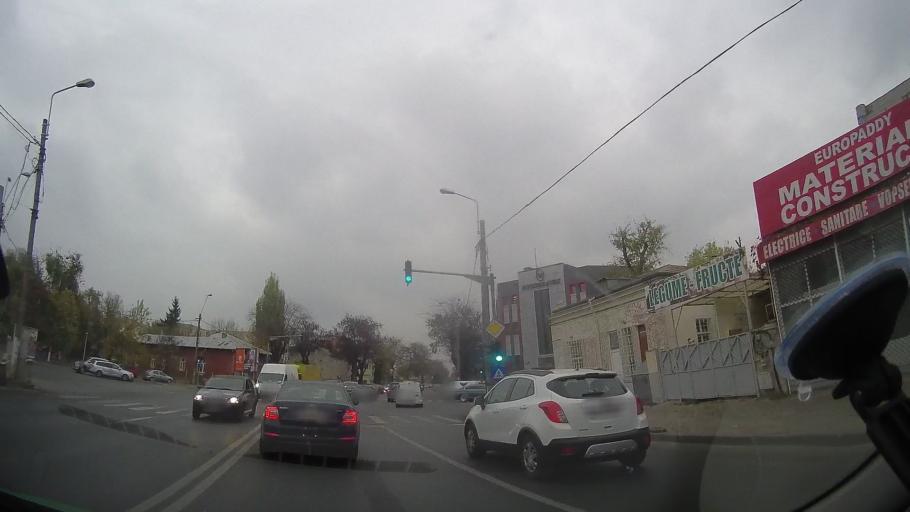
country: RO
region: Bucuresti
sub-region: Municipiul Bucuresti
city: Bucuresti
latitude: 44.4168
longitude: 26.0835
